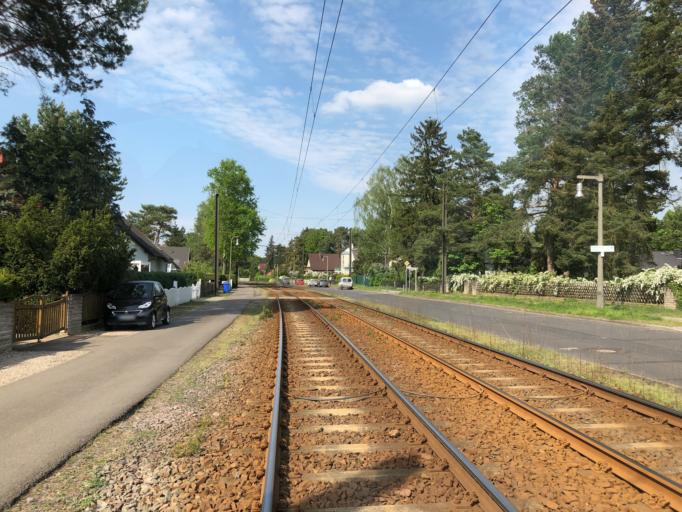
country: DE
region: Berlin
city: Schmockwitz
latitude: 52.3882
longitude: 13.6349
